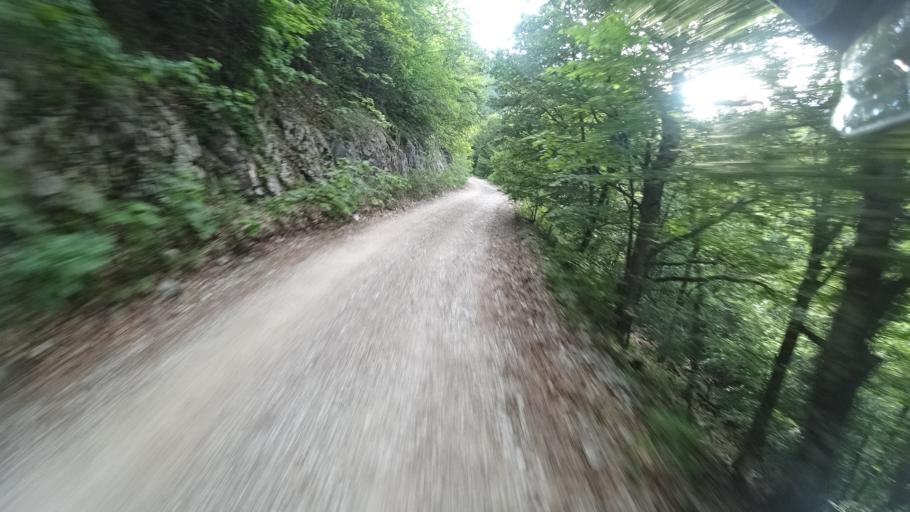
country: HR
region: Licko-Senjska
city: Gospic
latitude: 44.4686
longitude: 15.3061
